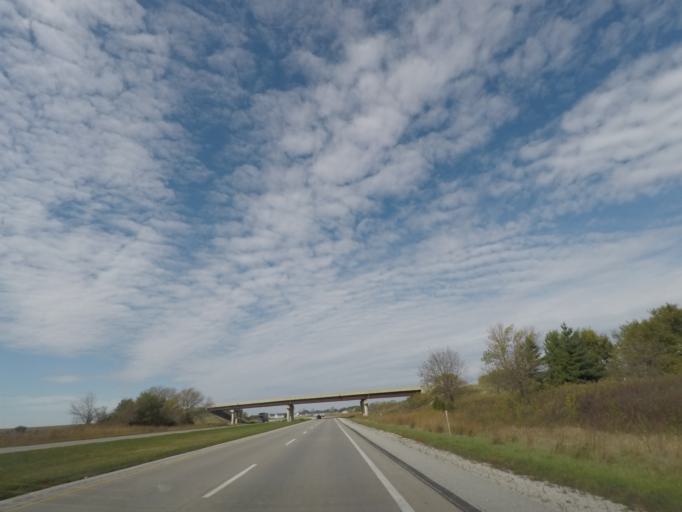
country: US
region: Iowa
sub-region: Story County
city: Ames
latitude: 42.0220
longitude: -93.7234
